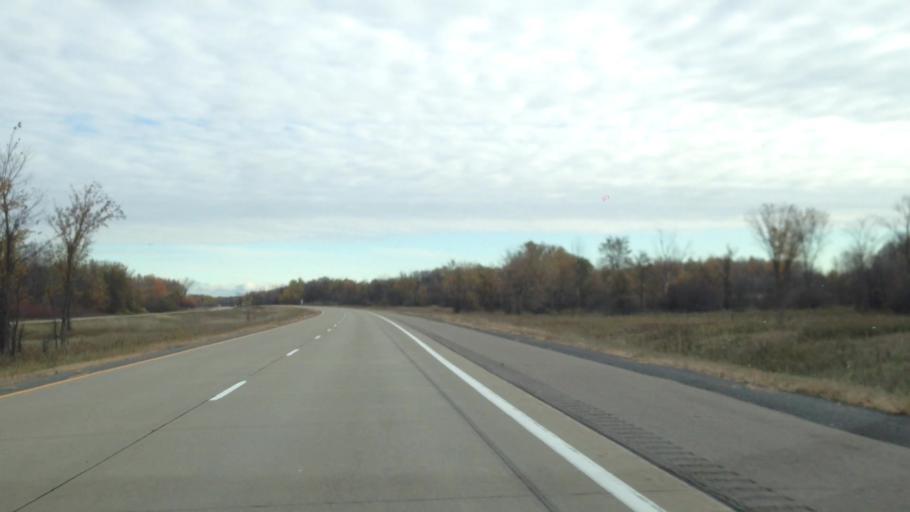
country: CA
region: Ontario
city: Hawkesbury
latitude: 45.3884
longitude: -74.7880
